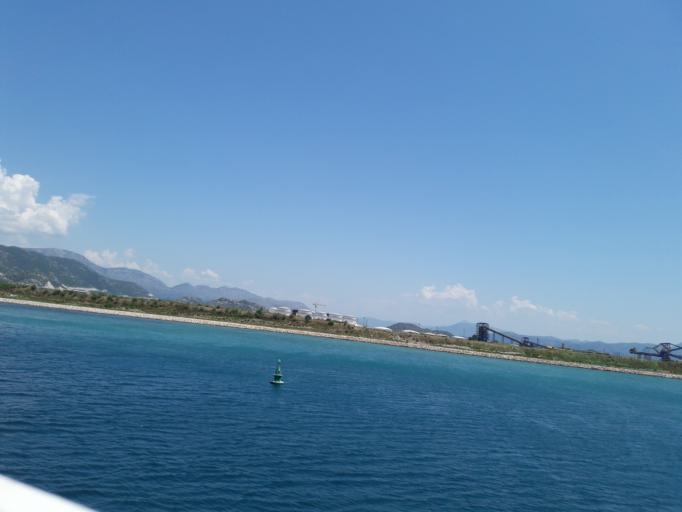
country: HR
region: Dubrovacko-Neretvanska
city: Komin
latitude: 43.0392
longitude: 17.4184
